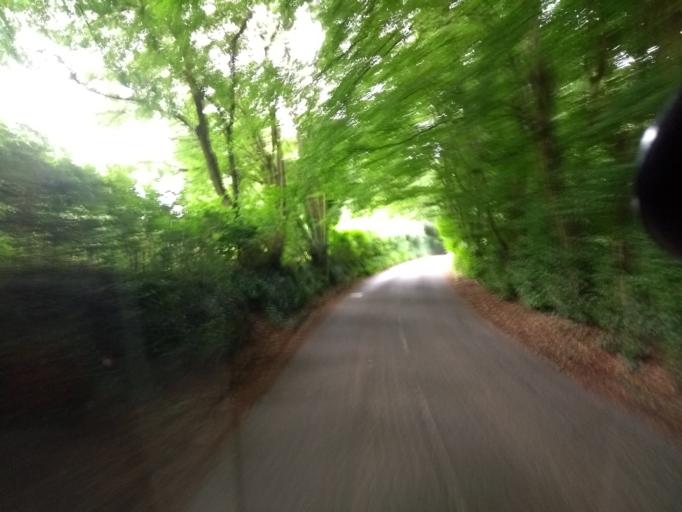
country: GB
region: England
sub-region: Somerset
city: Williton
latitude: 51.1279
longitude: -3.3232
